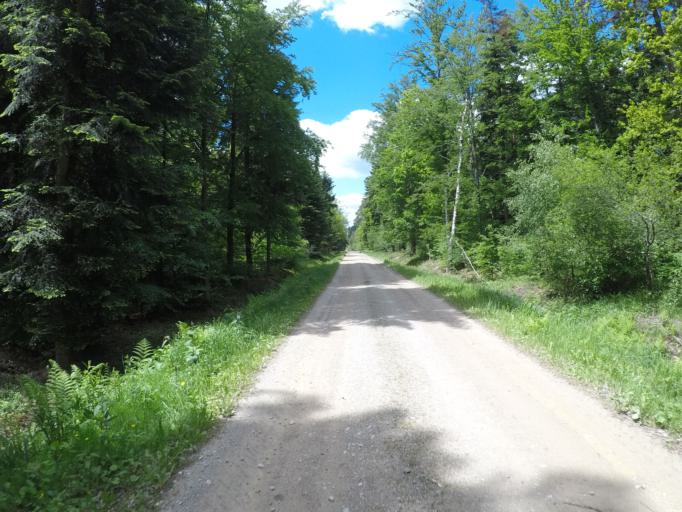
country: PL
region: Swietokrzyskie
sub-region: Powiat kielecki
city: Kostomloty Pierwsze
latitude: 50.9308
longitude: 20.6368
